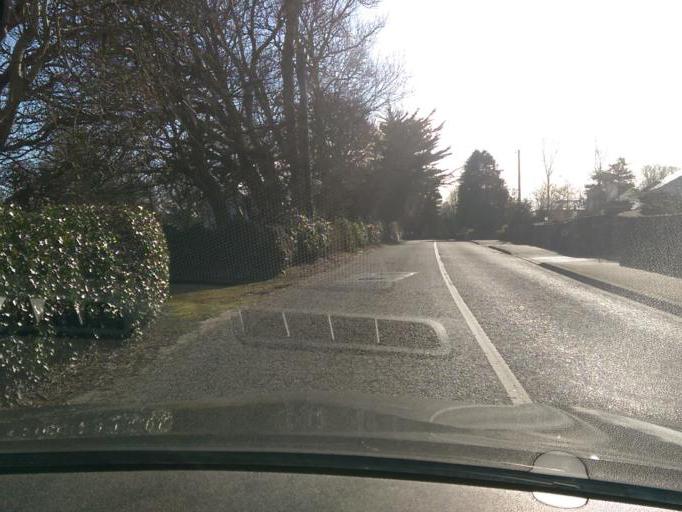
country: IE
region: Connaught
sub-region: County Galway
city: Oranmore
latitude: 53.2579
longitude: -8.9342
